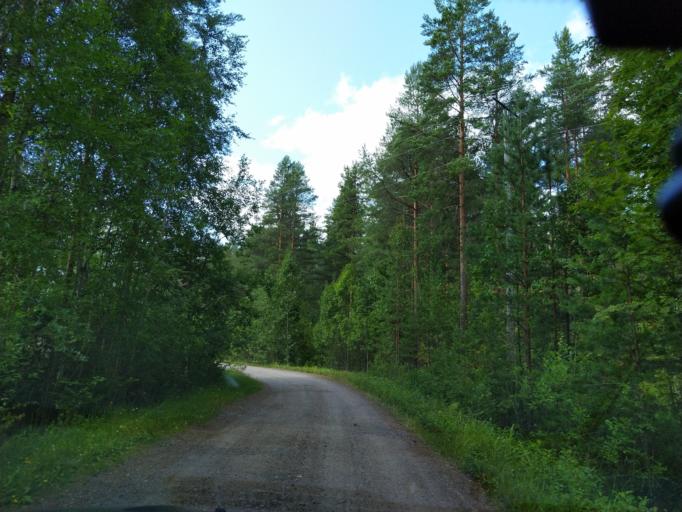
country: FI
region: Uusimaa
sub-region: Helsinki
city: Kaerkoelae
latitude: 60.7472
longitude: 24.1149
